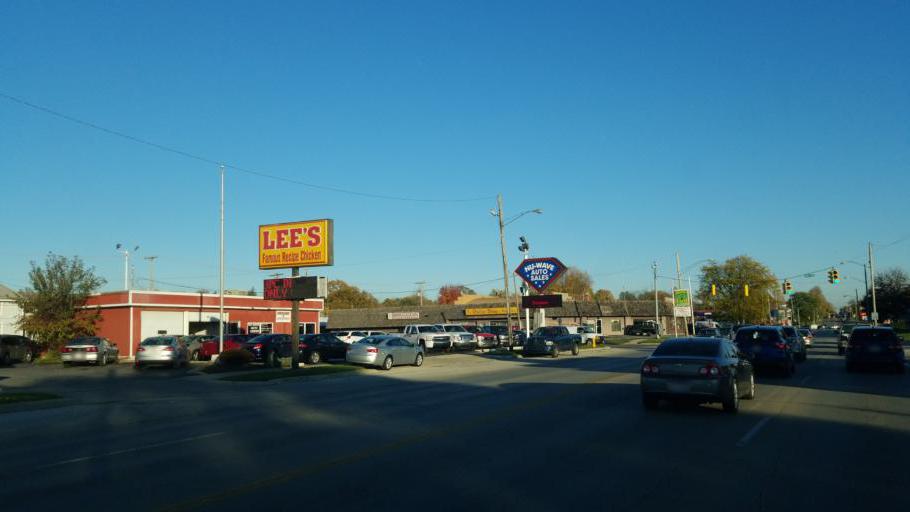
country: US
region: Ohio
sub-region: Sandusky County
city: Fremont
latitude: 41.3460
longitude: -83.1080
